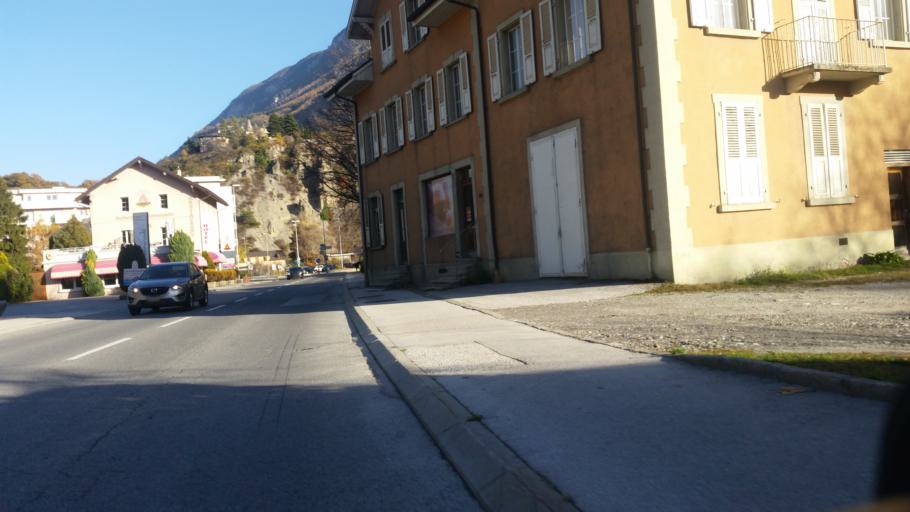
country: CH
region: Valais
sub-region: Sierre District
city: Chippis
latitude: 46.2847
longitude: 7.5378
